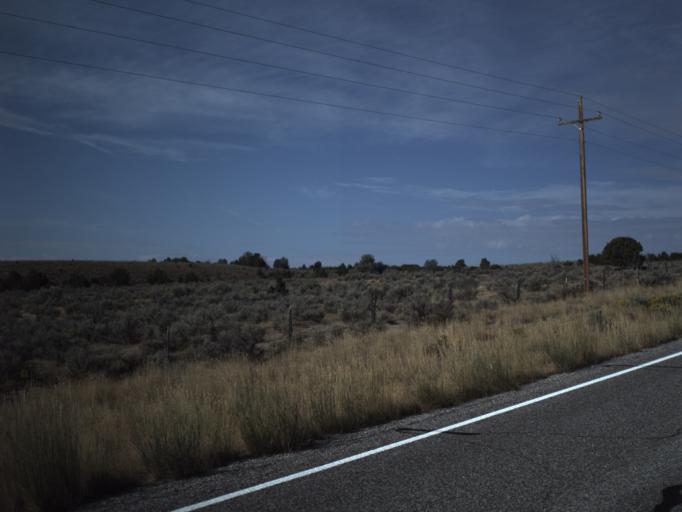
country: US
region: Idaho
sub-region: Cassia County
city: Burley
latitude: 41.8170
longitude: -113.2461
